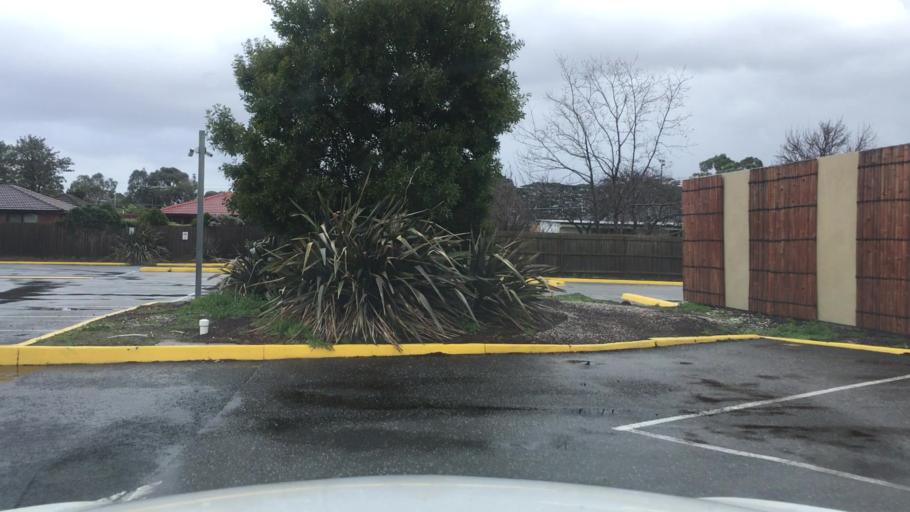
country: AU
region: Victoria
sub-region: Greater Dandenong
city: Springvale
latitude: -37.9461
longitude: 145.1463
